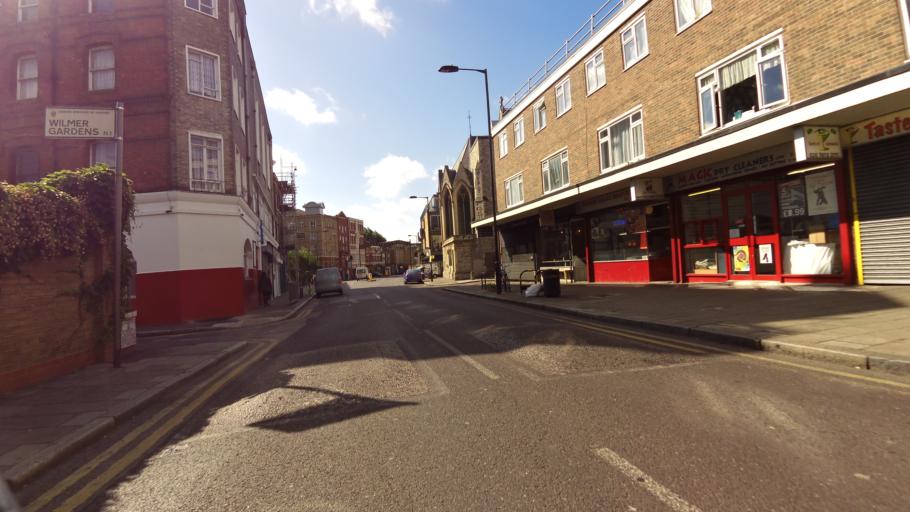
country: GB
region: England
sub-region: Greater London
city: Barbican
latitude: 51.5350
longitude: -0.0810
